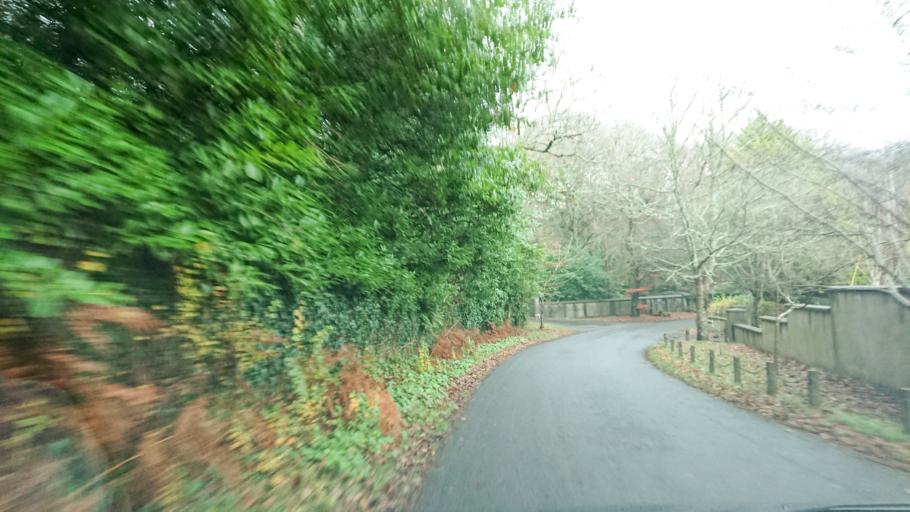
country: IE
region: Munster
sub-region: Waterford
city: Dunmore East
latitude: 52.2062
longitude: -7.0026
